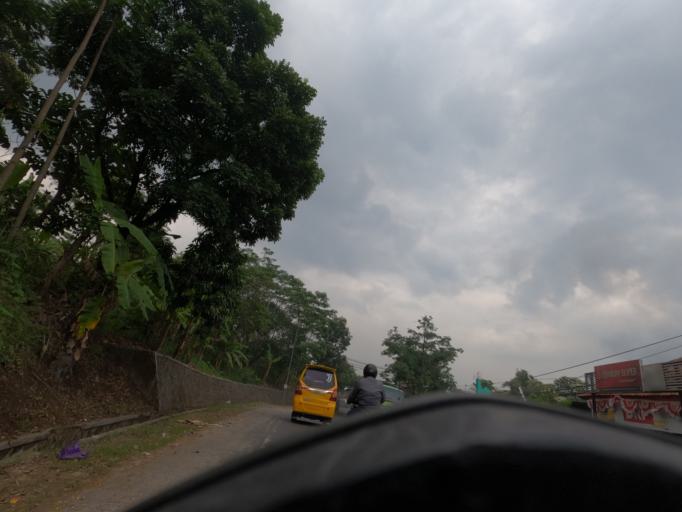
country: ID
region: West Java
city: Padalarang
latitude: -6.8309
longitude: 107.4416
